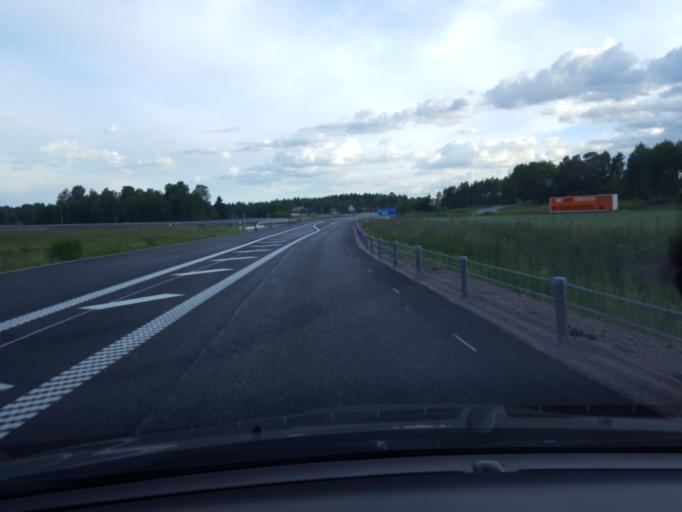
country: SE
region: Uppsala
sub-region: Osthammars Kommun
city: Gimo
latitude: 60.0829
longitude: 18.1167
